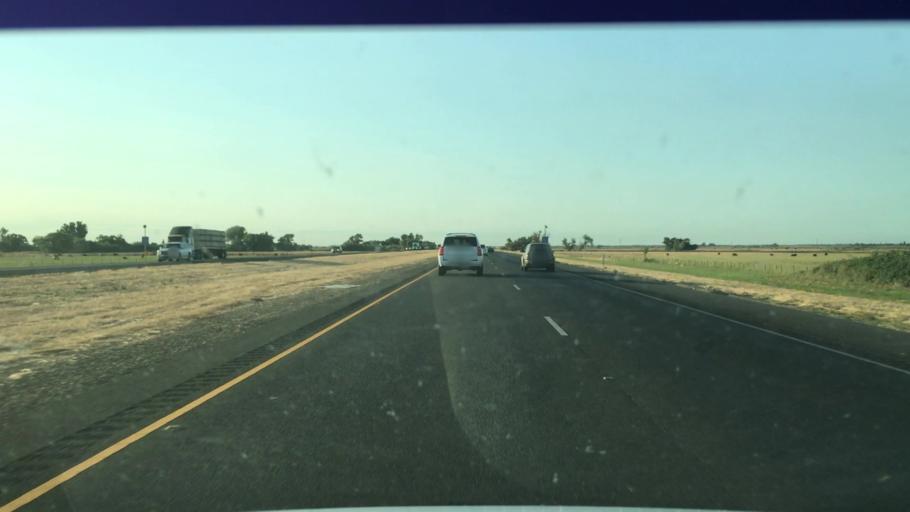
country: US
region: California
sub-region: Sacramento County
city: Laguna
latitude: 38.3391
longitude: -121.4691
